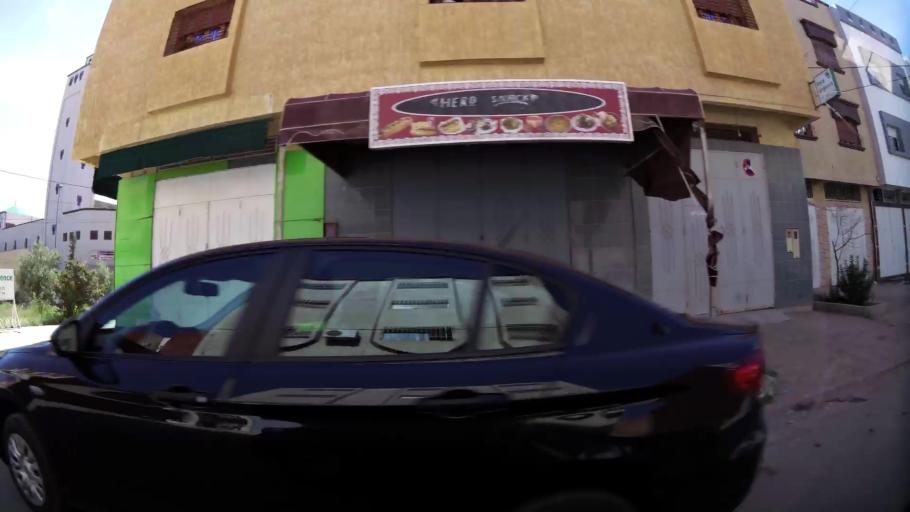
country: MA
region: Oriental
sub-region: Oujda-Angad
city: Oujda
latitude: 34.6572
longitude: -1.9141
